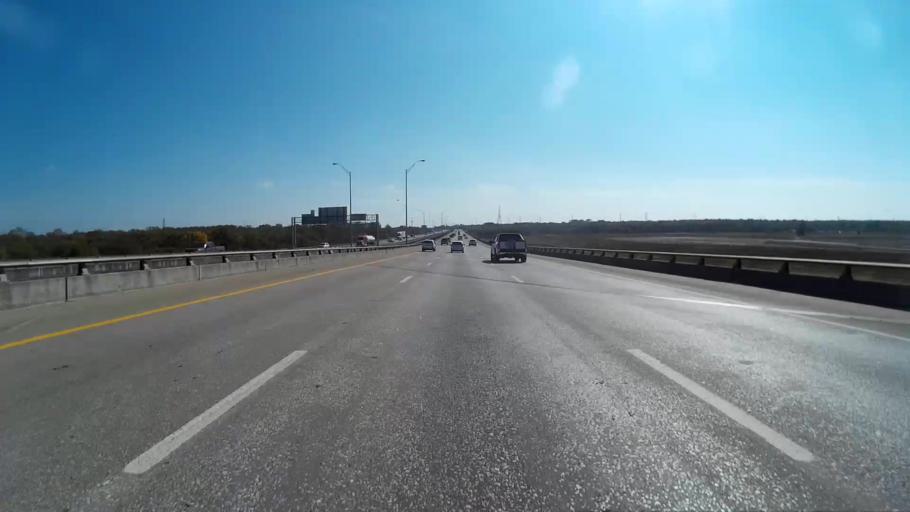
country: US
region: Texas
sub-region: Dallas County
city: Dallas
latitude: 32.7341
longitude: -96.7652
